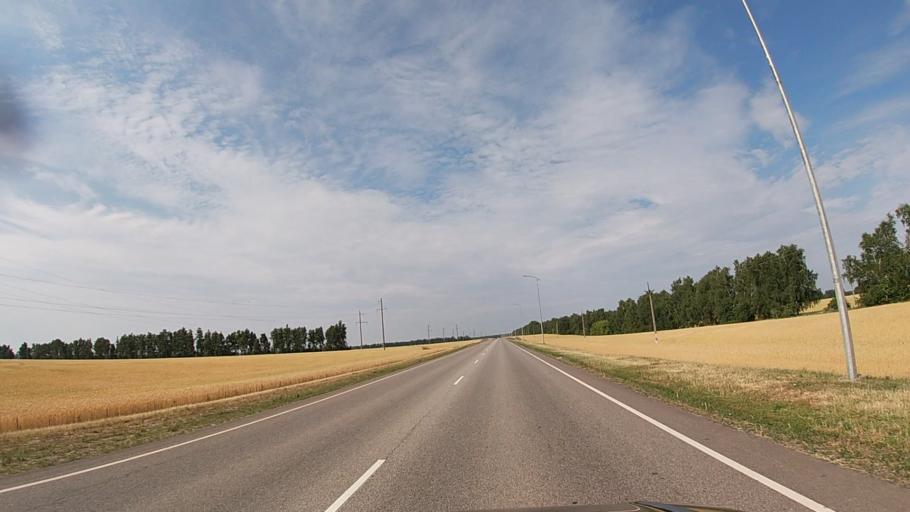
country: RU
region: Belgorod
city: Proletarskiy
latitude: 50.8231
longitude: 35.7585
